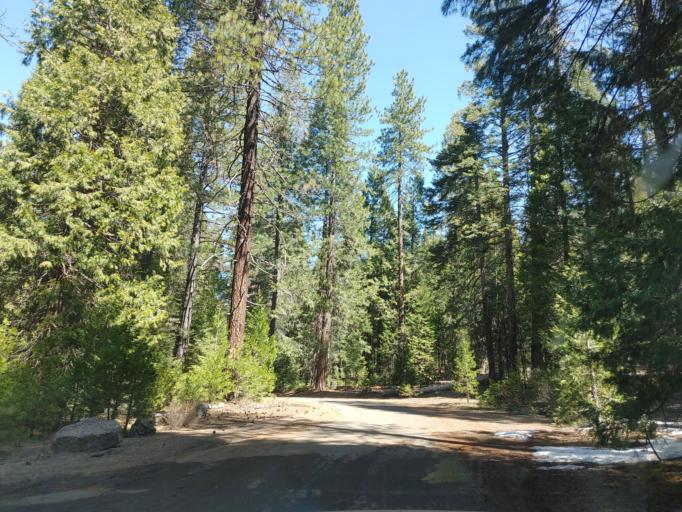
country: US
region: California
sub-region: Siskiyou County
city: McCloud
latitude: 41.2383
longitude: -122.0089
